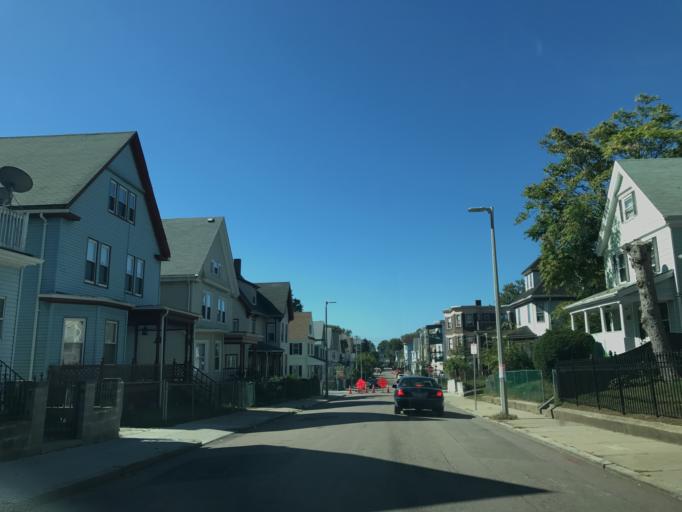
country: US
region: Massachusetts
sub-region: Suffolk County
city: South Boston
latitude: 42.2950
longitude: -71.0748
